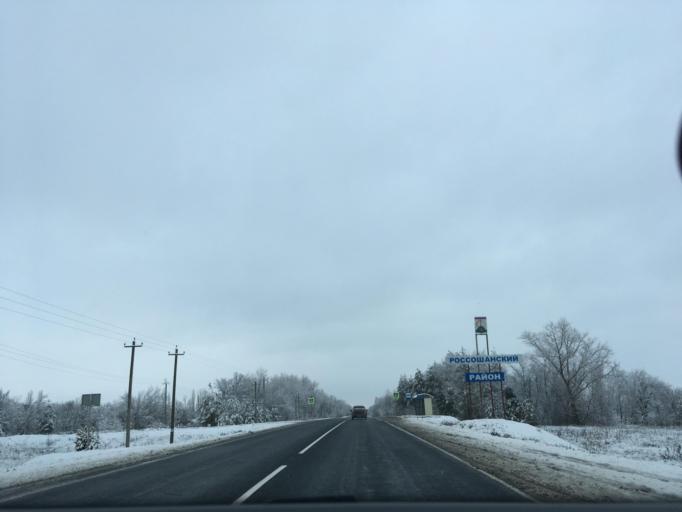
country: RU
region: Voronezj
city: Zabolotovka
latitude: 50.2289
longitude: 39.4070
